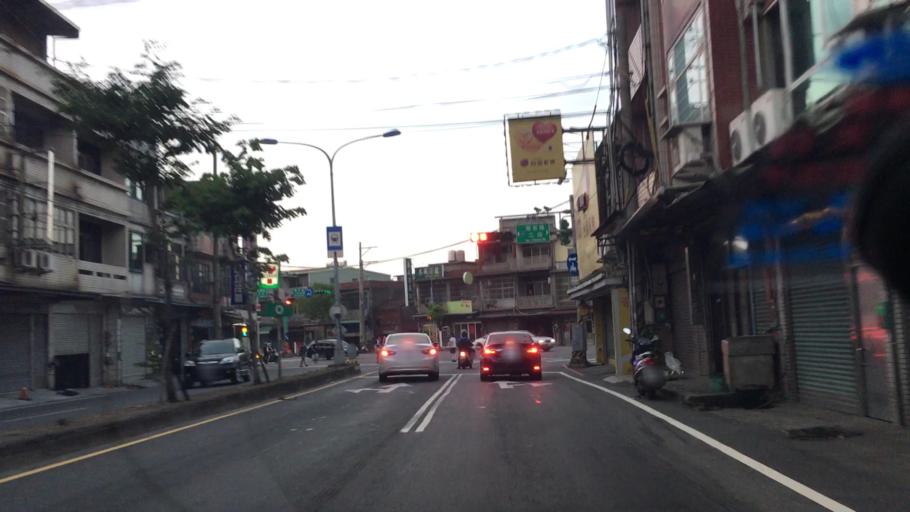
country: TW
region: Taiwan
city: Taoyuan City
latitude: 25.0621
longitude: 121.2669
